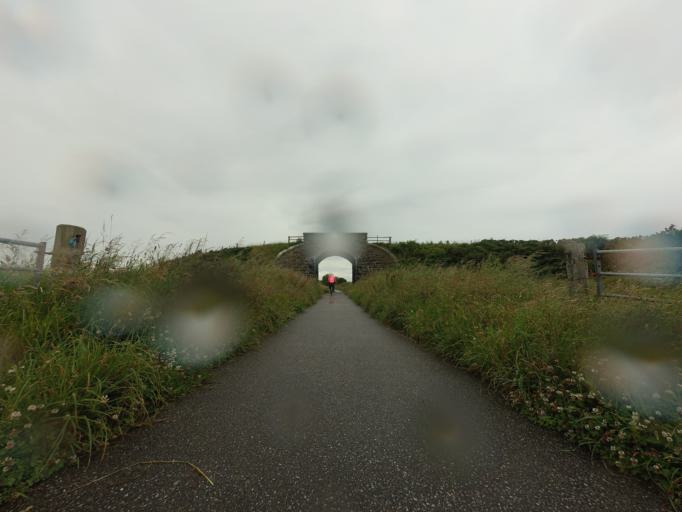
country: GB
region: Scotland
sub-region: Moray
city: Findochty
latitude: 57.6875
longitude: -2.9249
